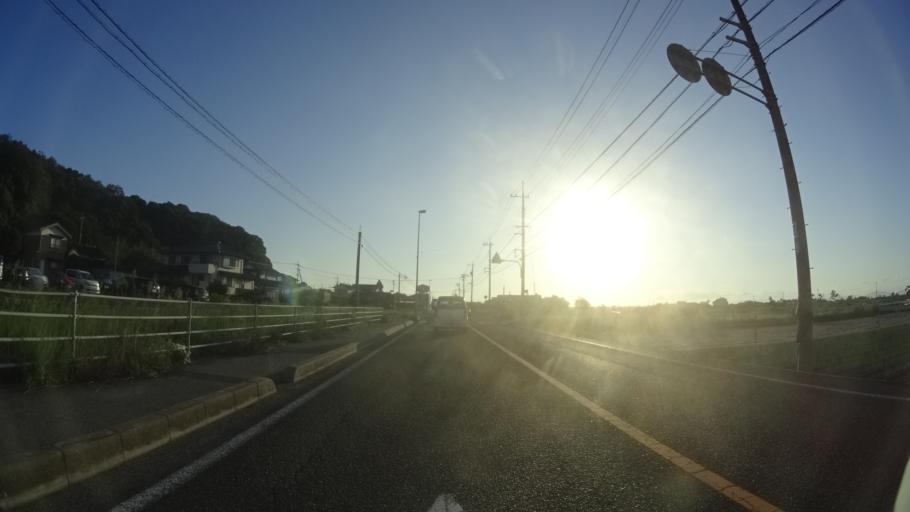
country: JP
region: Tottori
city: Yonago
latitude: 35.4509
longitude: 133.4119
